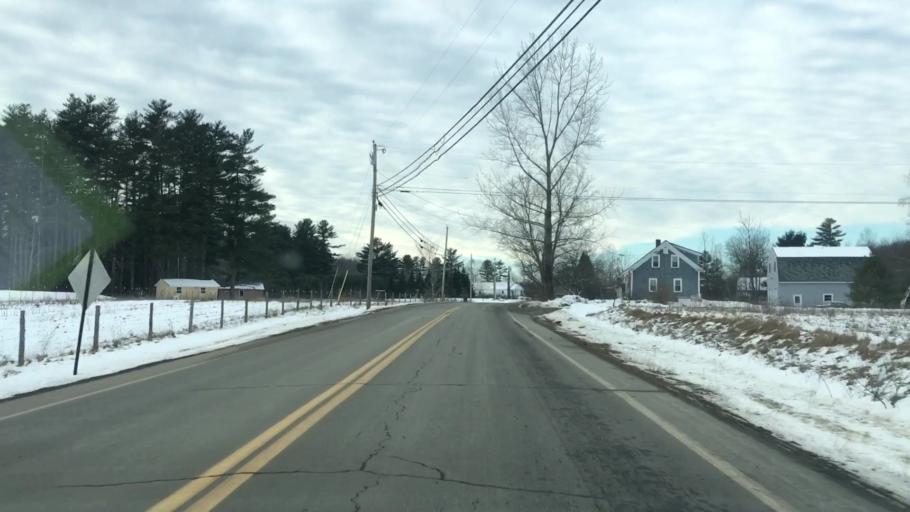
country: US
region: Maine
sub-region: Lincoln County
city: Whitefield
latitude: 44.2226
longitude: -69.5966
